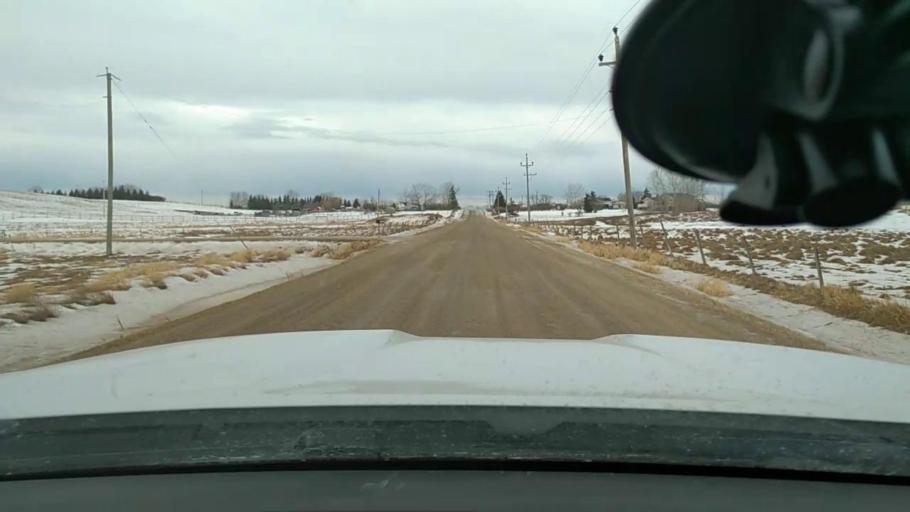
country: CA
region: Alberta
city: Airdrie
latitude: 51.2417
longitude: -113.9289
